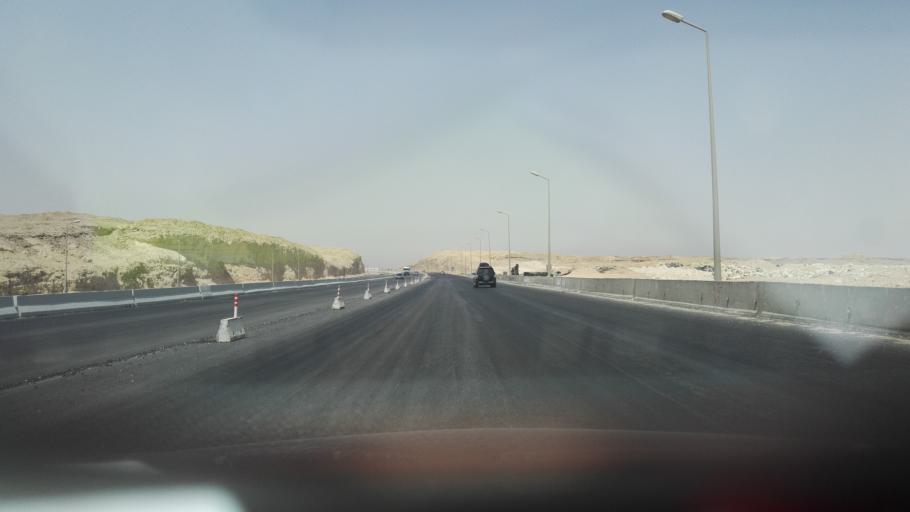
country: EG
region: As Suways
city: Ain Sukhna
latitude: 29.6801
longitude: 32.2198
